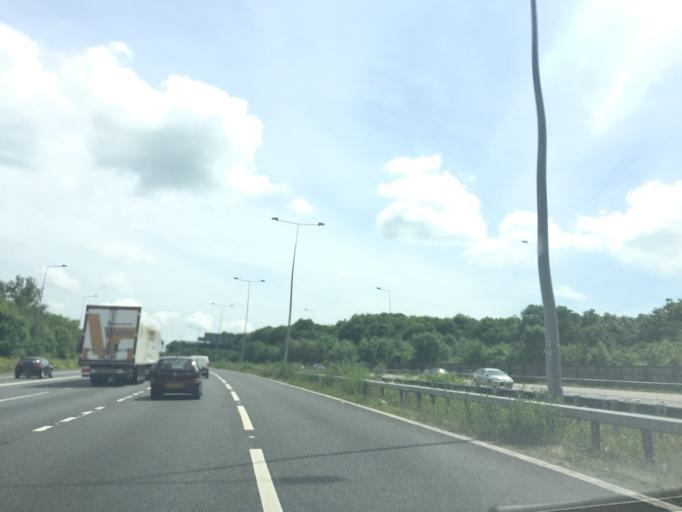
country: GB
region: England
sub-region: Kent
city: Boxley
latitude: 51.3306
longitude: 0.5140
